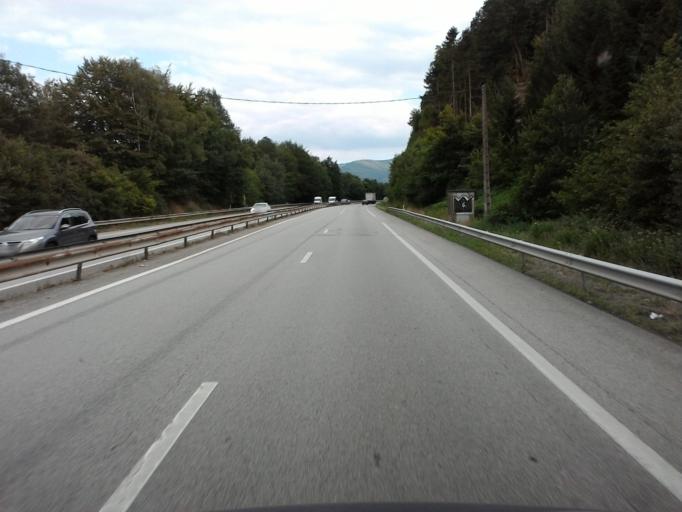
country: FR
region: Lorraine
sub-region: Departement des Vosges
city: Eloyes
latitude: 48.0924
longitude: 6.5945
